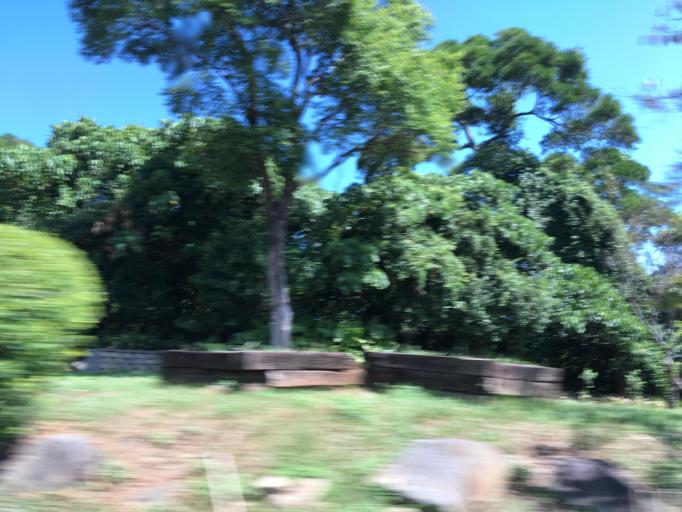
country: TW
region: Taipei
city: Taipei
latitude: 25.1500
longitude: 121.5045
